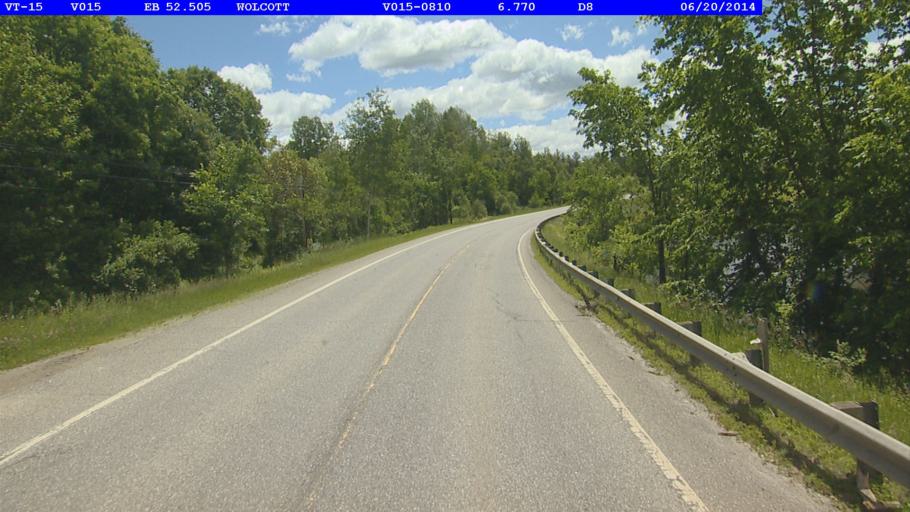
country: US
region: Vermont
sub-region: Caledonia County
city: Hardwick
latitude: 44.5281
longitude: -72.4215
